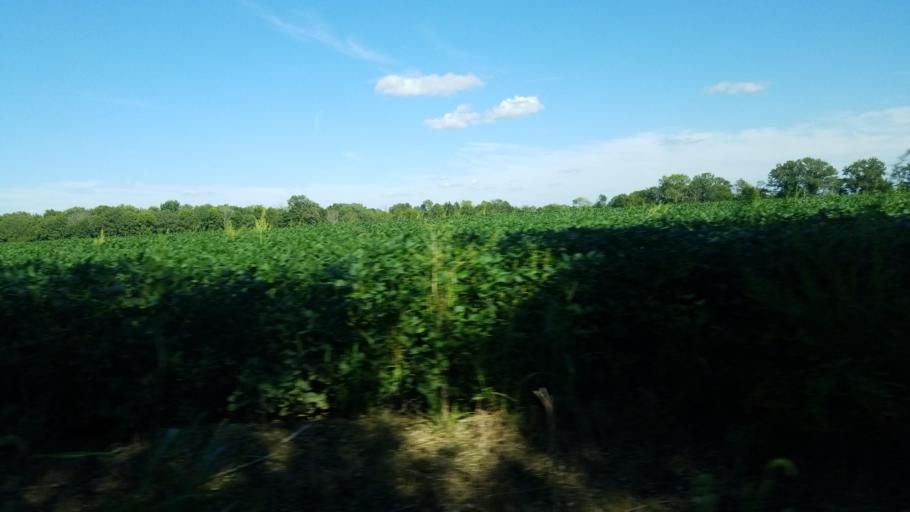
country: US
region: Illinois
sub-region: Saline County
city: Harrisburg
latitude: 37.8156
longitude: -88.5672
